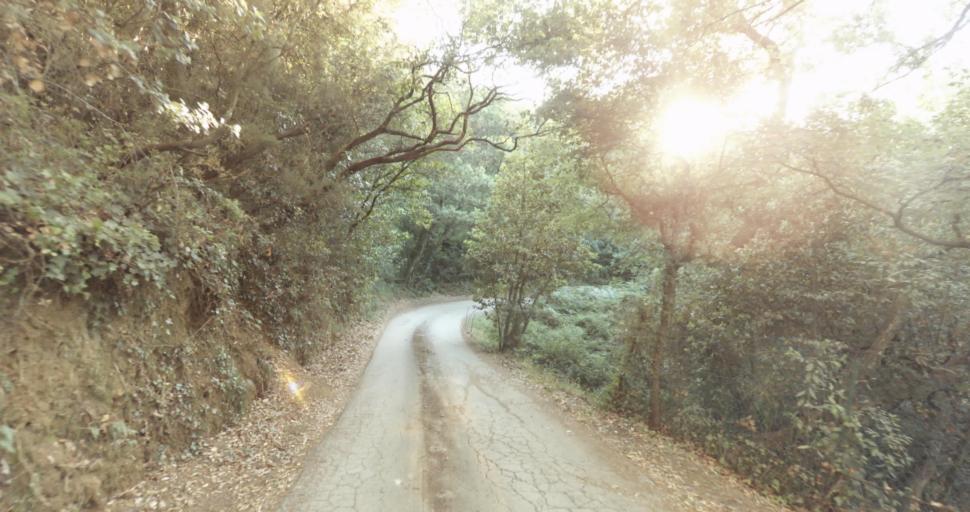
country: FR
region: Provence-Alpes-Cote d'Azur
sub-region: Departement du Var
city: Gassin
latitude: 43.2232
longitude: 6.5914
